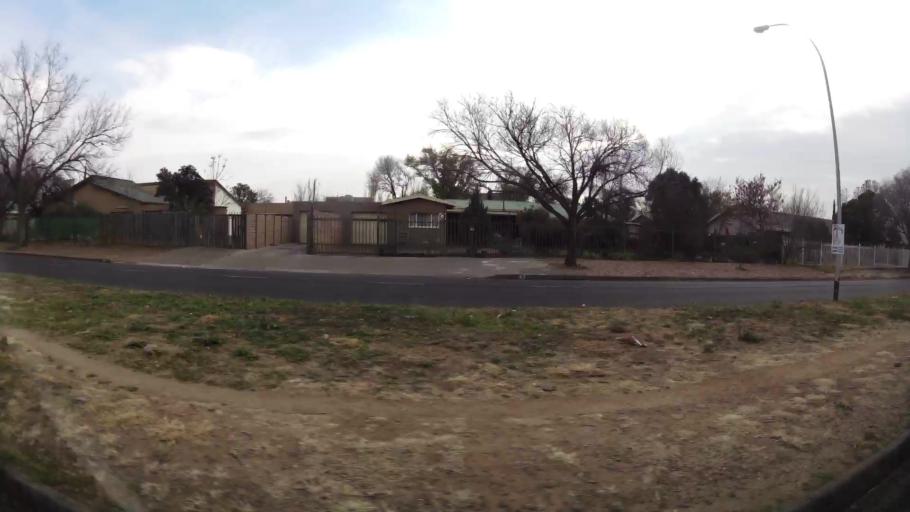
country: ZA
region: Orange Free State
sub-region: Mangaung Metropolitan Municipality
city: Bloemfontein
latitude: -29.1233
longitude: 26.1857
